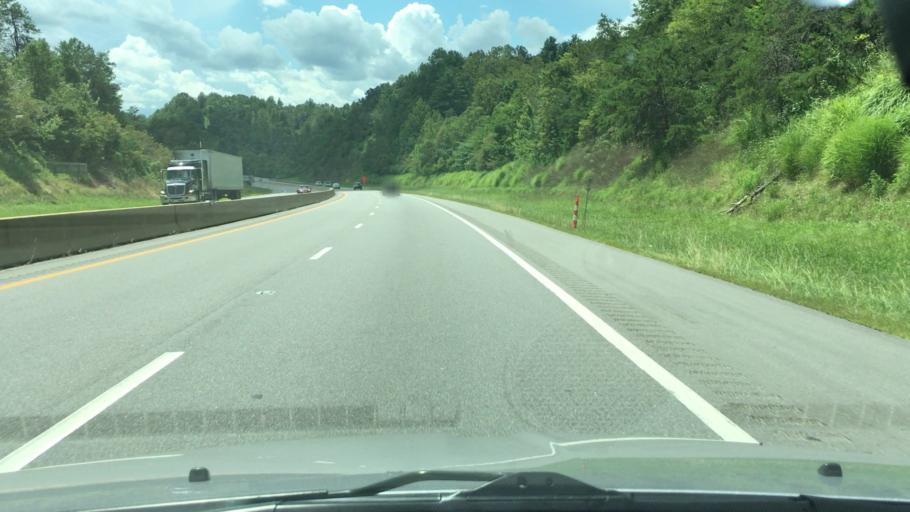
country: US
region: North Carolina
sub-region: Madison County
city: Mars Hill
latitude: 35.7967
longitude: -82.5387
